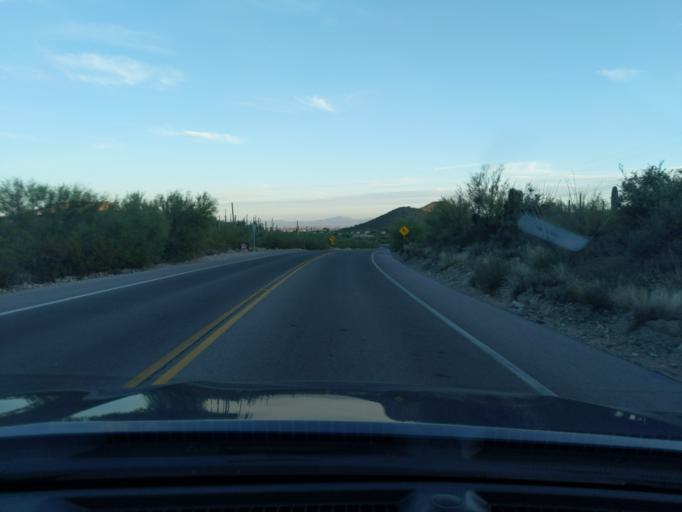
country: US
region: Arizona
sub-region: Pima County
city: Tucson Estates
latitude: 32.2280
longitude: -111.0398
